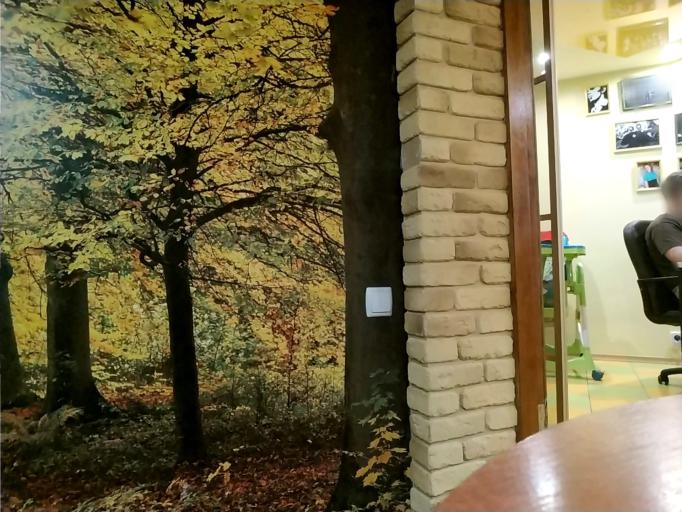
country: RU
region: Tverskaya
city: Zapadnaya Dvina
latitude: 56.3315
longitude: 31.8856
